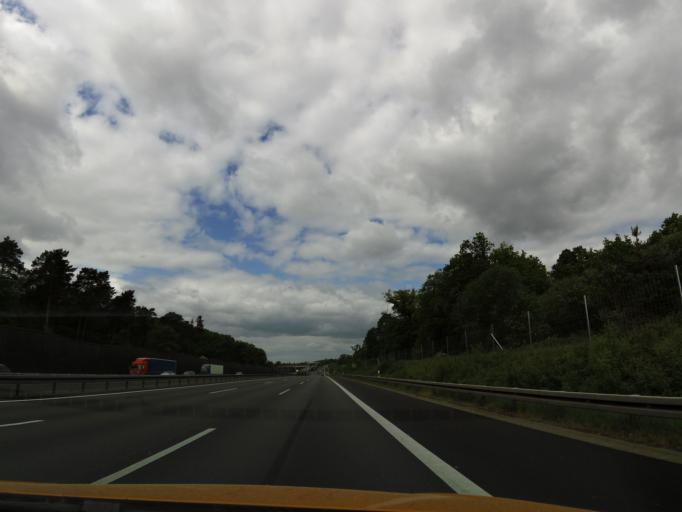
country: DE
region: Lower Saxony
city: Helmstedt
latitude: 52.2280
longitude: 11.0362
